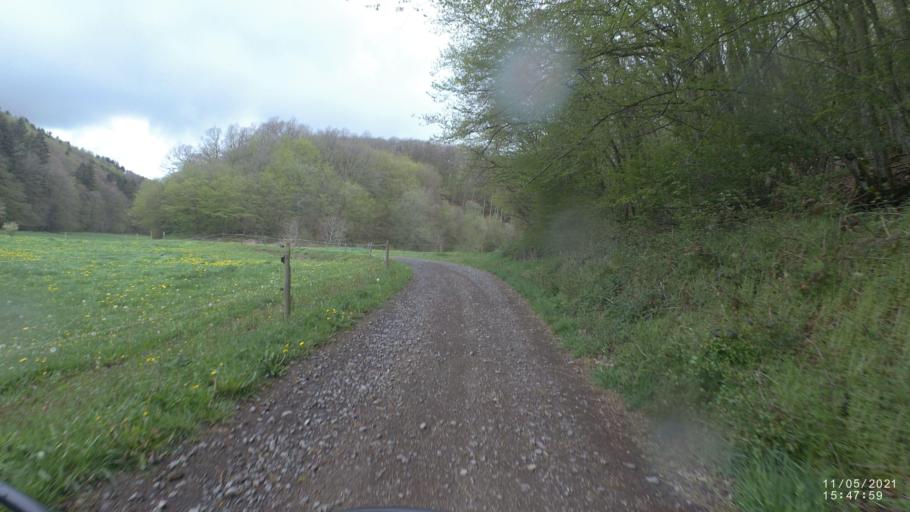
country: DE
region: Rheinland-Pfalz
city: Ditscheid
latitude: 50.3076
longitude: 7.0679
